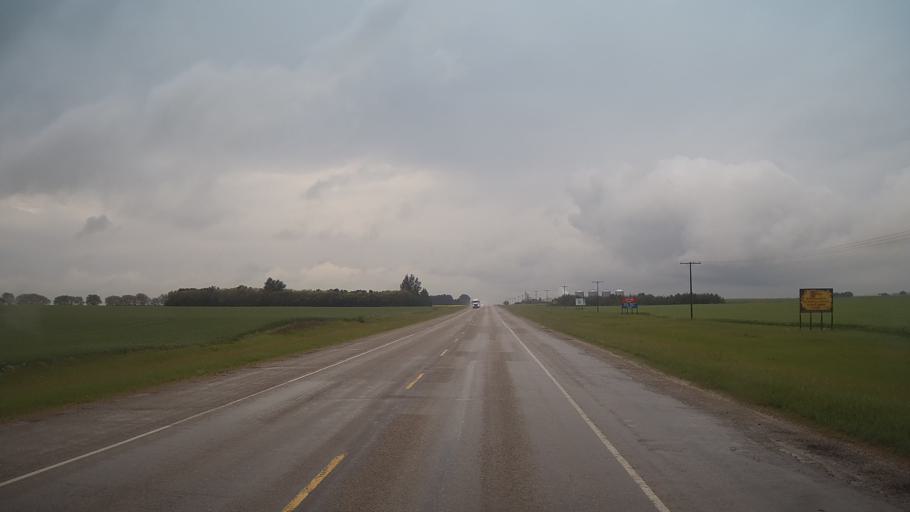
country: CA
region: Saskatchewan
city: Unity
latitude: 52.4350
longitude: -109.0787
